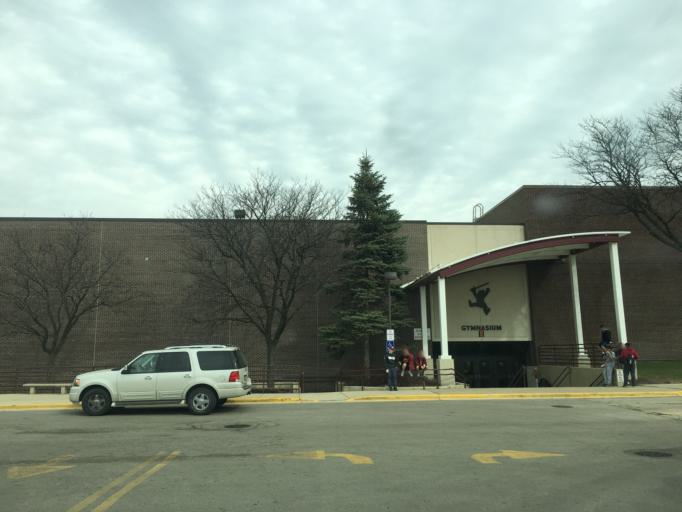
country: US
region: Illinois
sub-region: Cook County
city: Schaumburg
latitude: 42.0265
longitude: -88.1080
